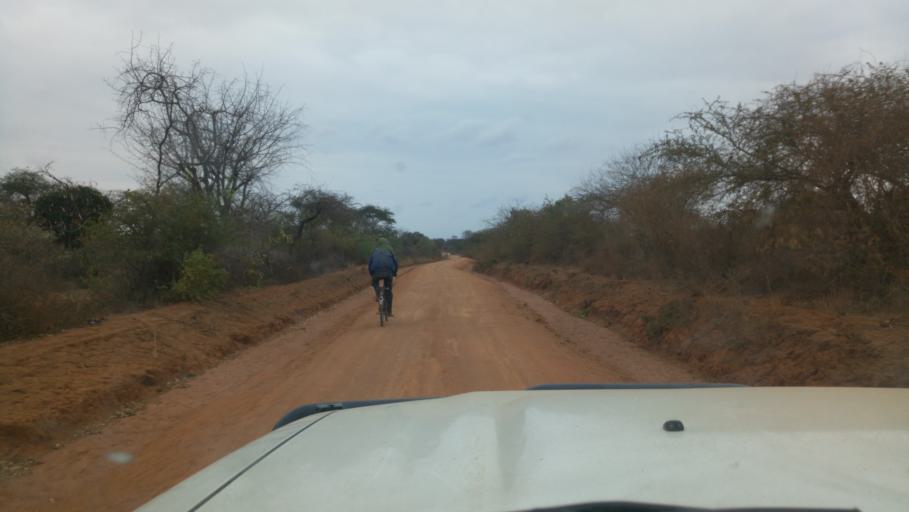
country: KE
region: Kitui
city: Kitui
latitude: -1.8701
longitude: 38.1750
